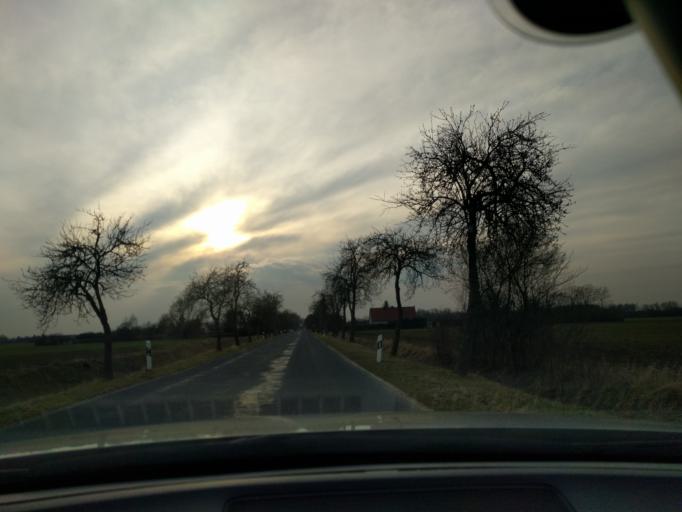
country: DE
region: Saxony-Anhalt
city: Iden
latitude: 52.8199
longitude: 11.9697
